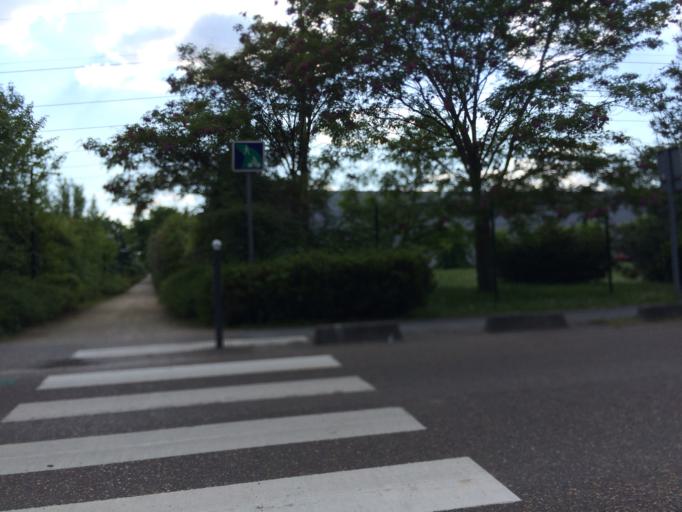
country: FR
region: Ile-de-France
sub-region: Departement de l'Essonne
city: Grigny
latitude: 48.6435
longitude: 2.3979
